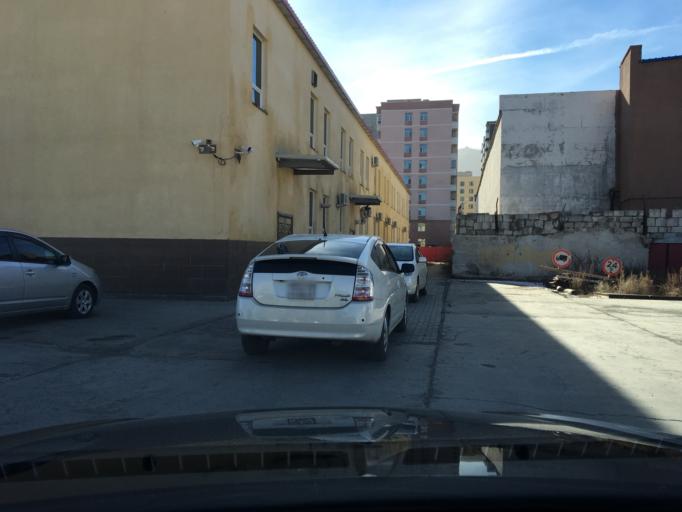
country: MN
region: Ulaanbaatar
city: Ulaanbaatar
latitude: 47.8927
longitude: 106.8942
